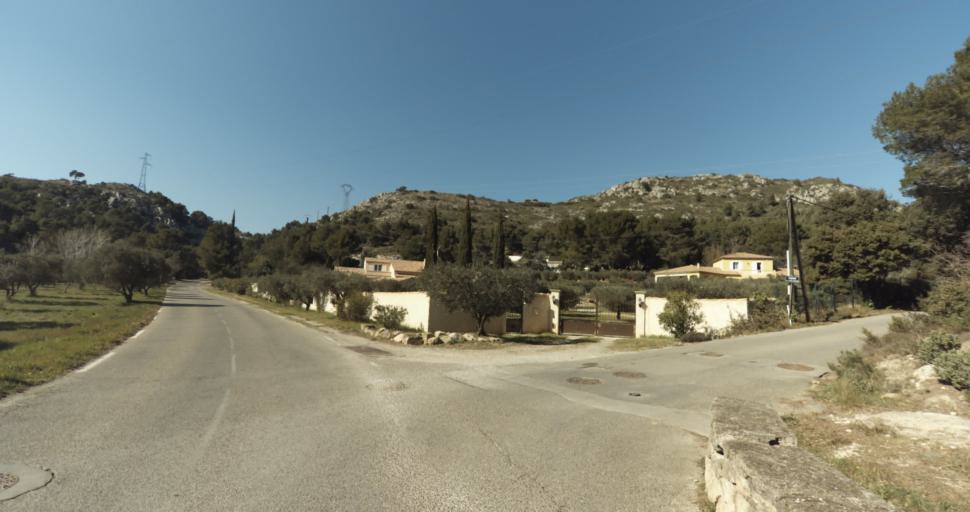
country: FR
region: Provence-Alpes-Cote d'Azur
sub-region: Departement des Bouches-du-Rhone
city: Pelissanne
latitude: 43.6482
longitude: 5.1561
